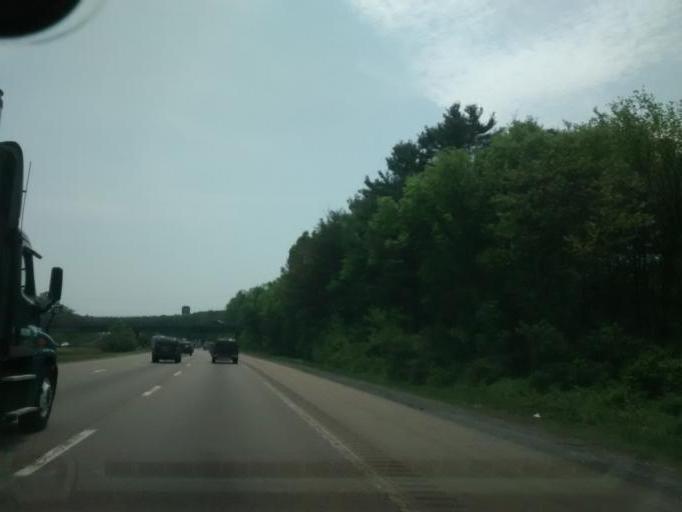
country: US
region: Massachusetts
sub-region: Norfolk County
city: Wrentham
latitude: 42.0450
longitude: -71.3595
